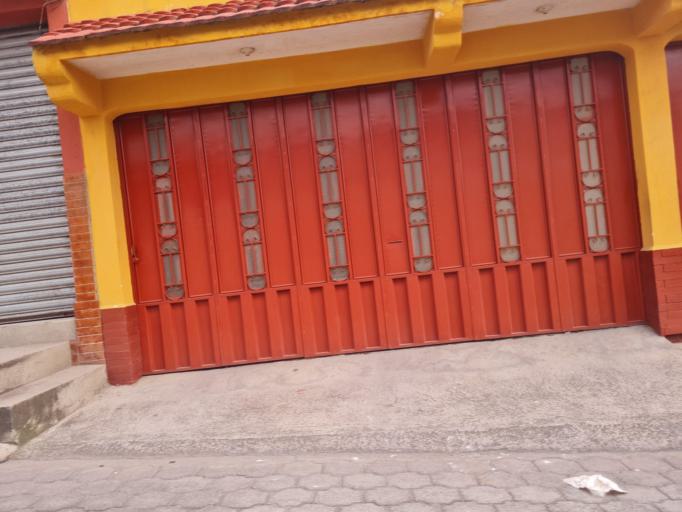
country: GT
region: Quetzaltenango
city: Quetzaltenango
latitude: 14.8366
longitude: -91.5352
